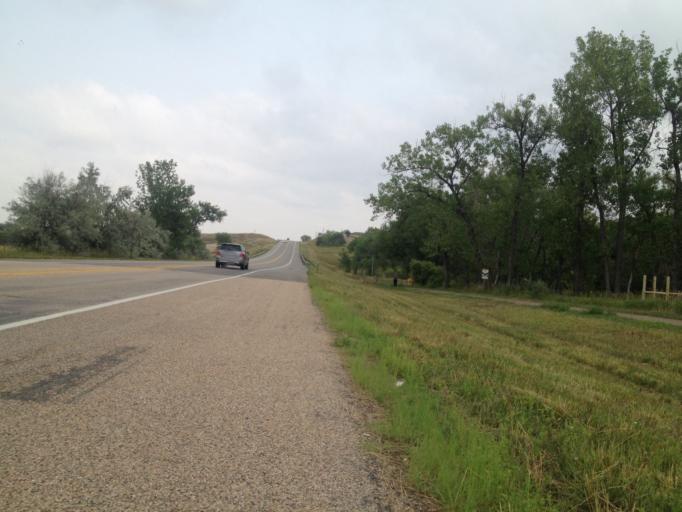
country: US
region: Colorado
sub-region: Boulder County
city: Louisville
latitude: 39.9725
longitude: -105.1237
